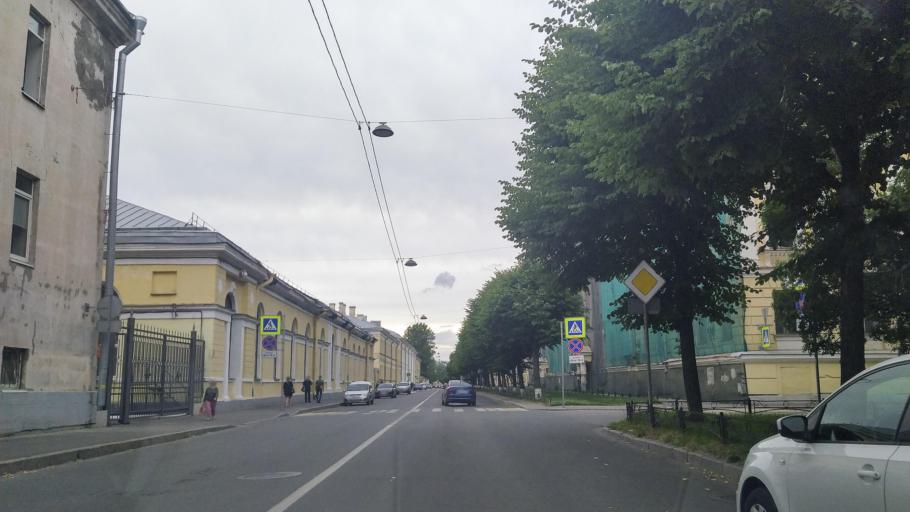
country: RU
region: St.-Petersburg
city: Petrogradka
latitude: 59.9567
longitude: 30.2888
